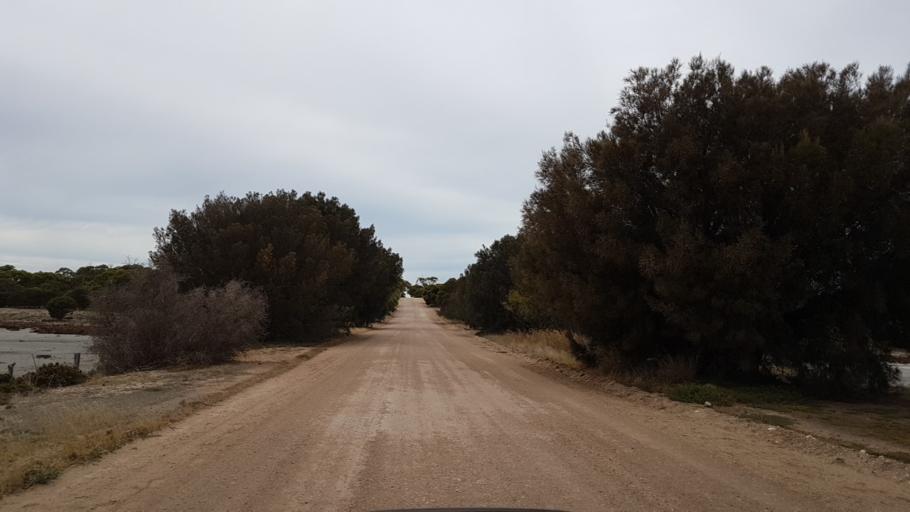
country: AU
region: South Australia
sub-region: Yorke Peninsula
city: Port Victoria
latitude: -34.7776
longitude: 137.5975
